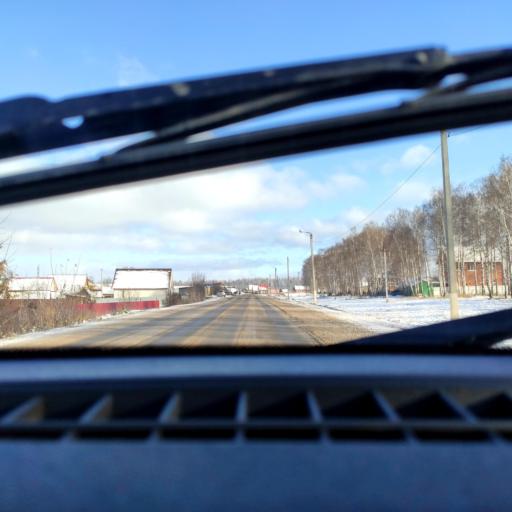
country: RU
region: Bashkortostan
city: Iglino
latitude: 54.8217
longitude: 56.4125
